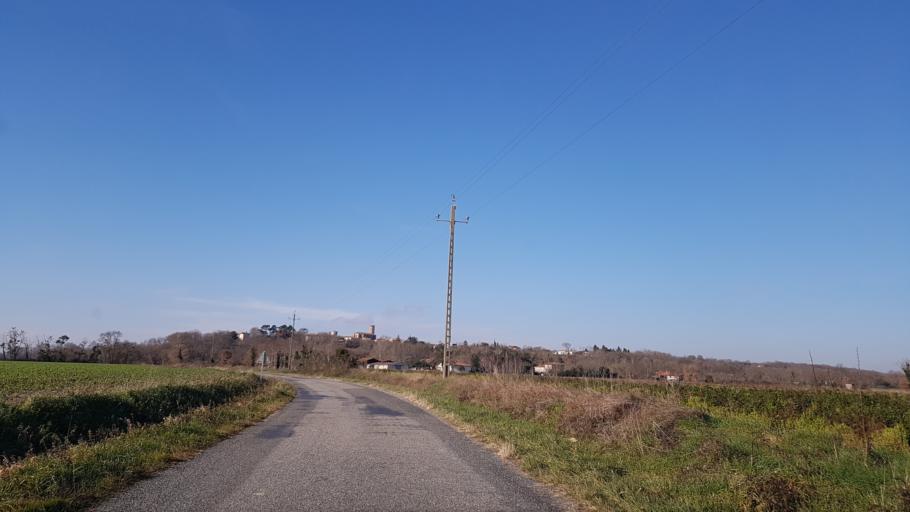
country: FR
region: Midi-Pyrenees
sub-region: Departement de l'Ariege
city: Mazeres
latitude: 43.1817
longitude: 1.6509
